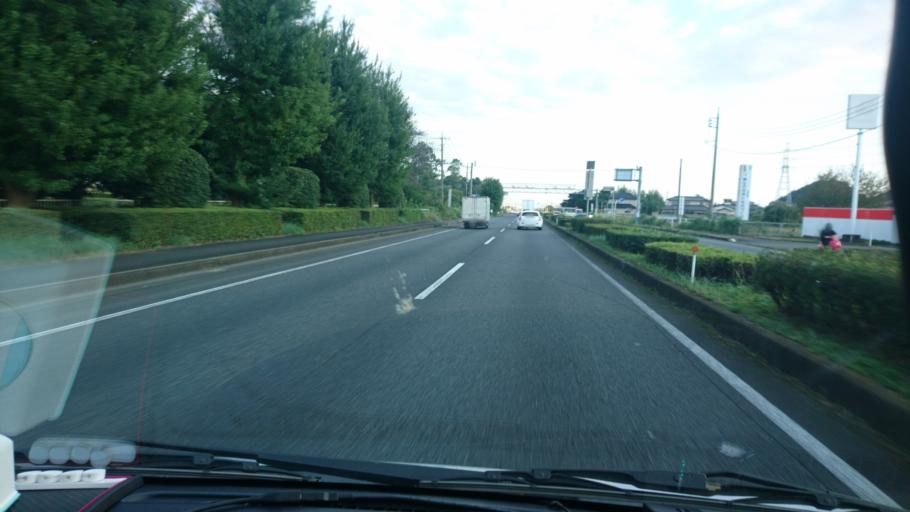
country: JP
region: Gunma
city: Kiryu
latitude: 36.3637
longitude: 139.3667
